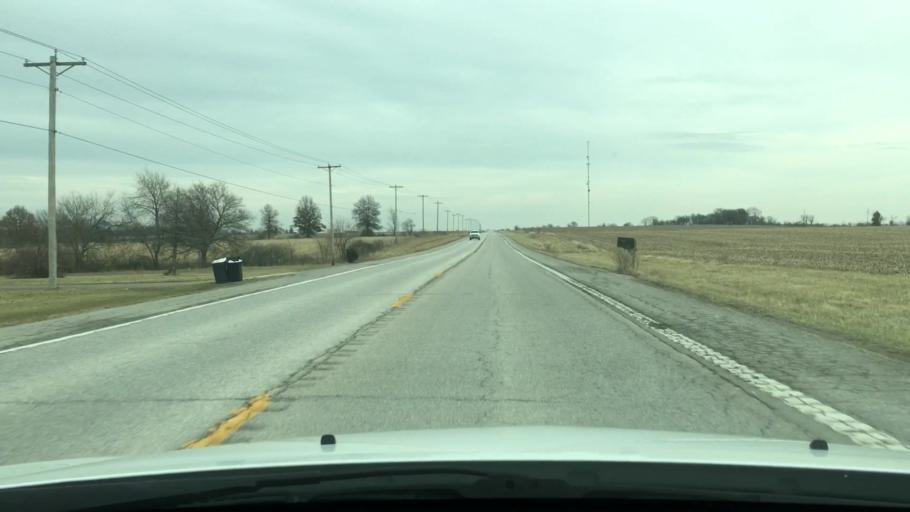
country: US
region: Missouri
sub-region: Pike County
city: Bowling Green
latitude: 39.3449
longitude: -91.3200
